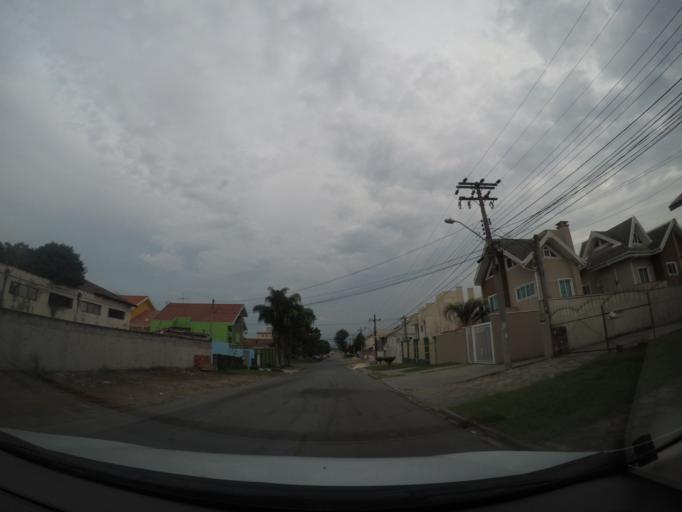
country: BR
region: Parana
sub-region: Sao Jose Dos Pinhais
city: Sao Jose dos Pinhais
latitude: -25.5140
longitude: -49.2328
